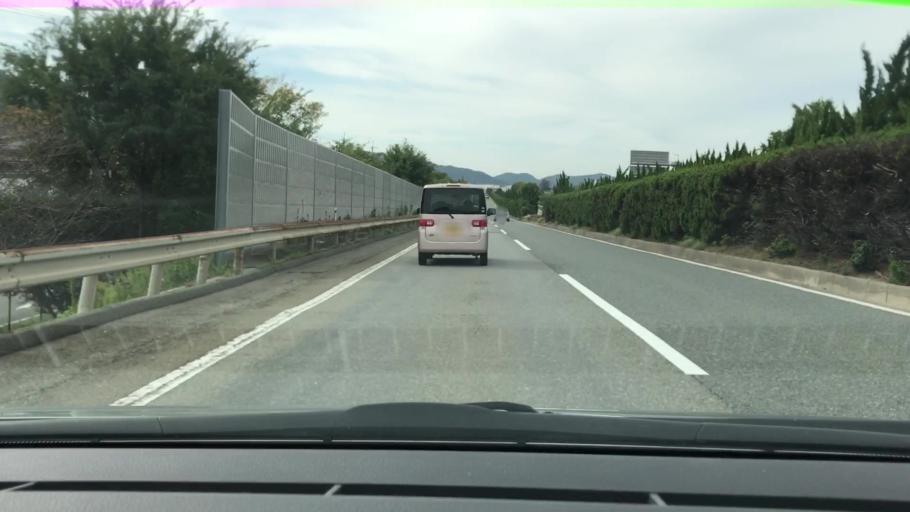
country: JP
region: Hyogo
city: Himeji
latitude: 34.9065
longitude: 134.7532
